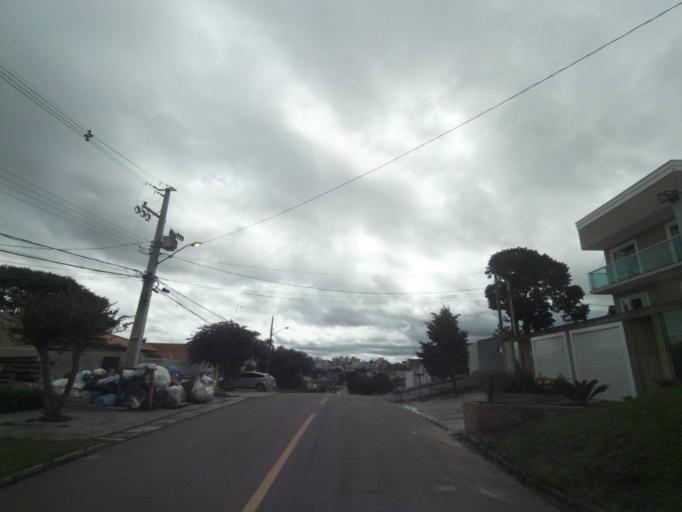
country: BR
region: Parana
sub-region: Curitiba
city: Curitiba
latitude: -25.4776
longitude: -49.2793
